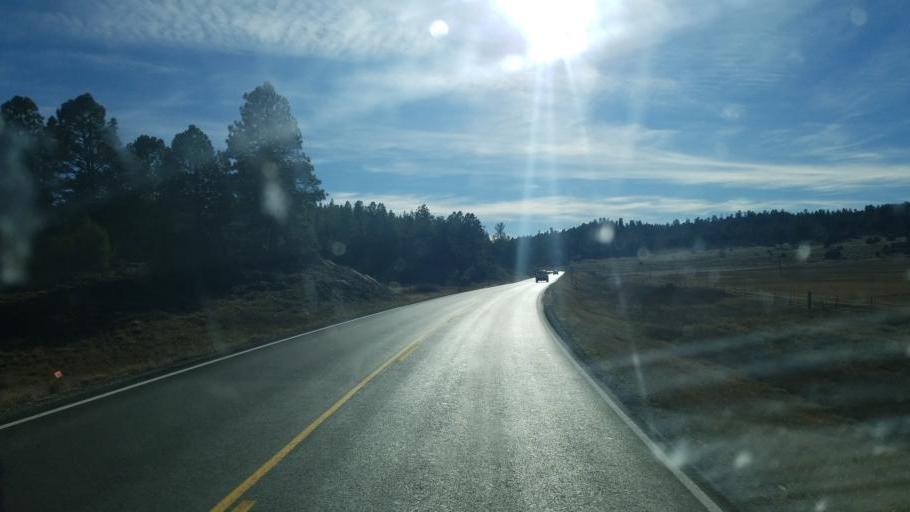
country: US
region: New Mexico
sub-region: Rio Arriba County
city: Dulce
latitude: 36.8579
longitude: -107.0045
